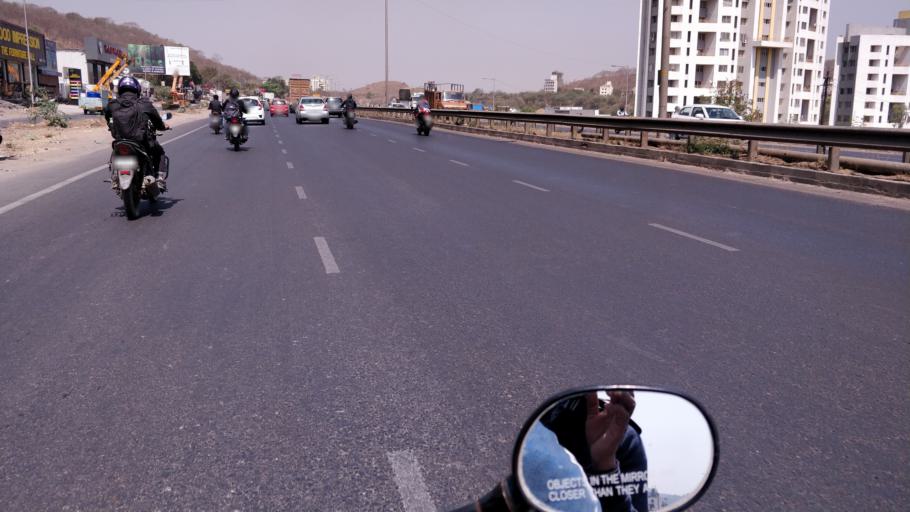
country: IN
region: Maharashtra
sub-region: Pune Division
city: Shivaji Nagar
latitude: 18.5411
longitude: 73.7788
